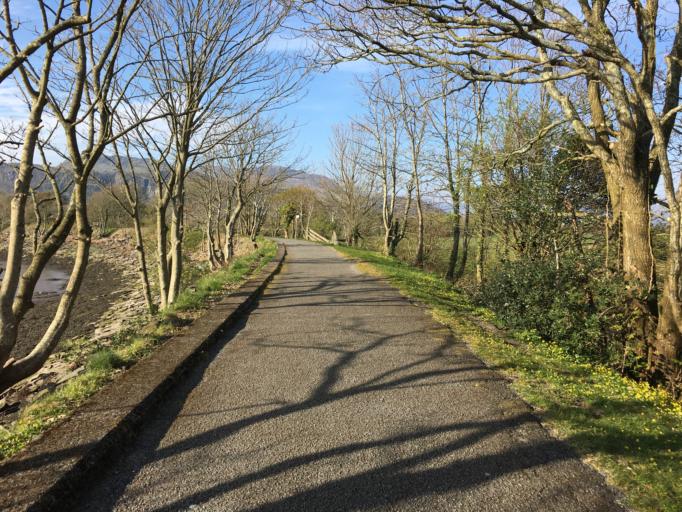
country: GB
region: Wales
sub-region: Gwynedd
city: Porthmadog
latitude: 52.9274
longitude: -4.1232
